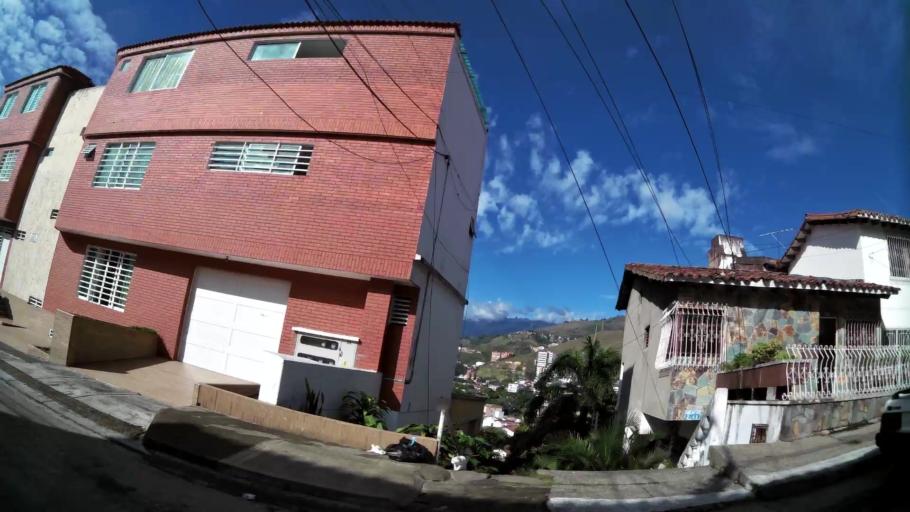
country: CO
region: Valle del Cauca
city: Cali
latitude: 3.4398
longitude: -76.5424
